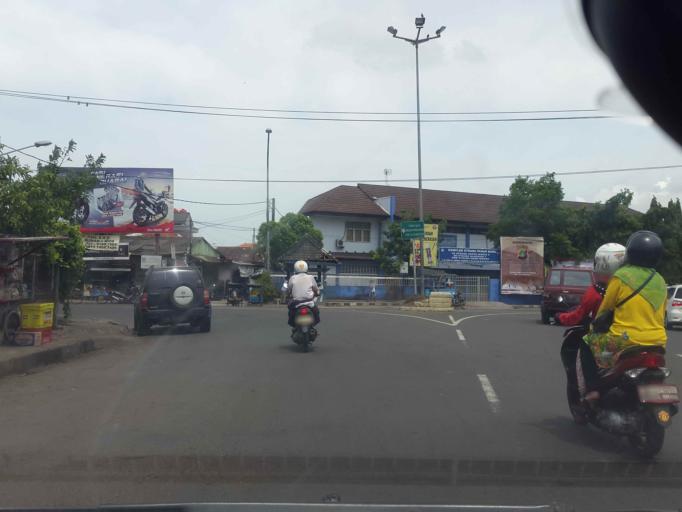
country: ID
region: Banten
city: Tangerang
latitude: -6.1705
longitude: 106.6254
